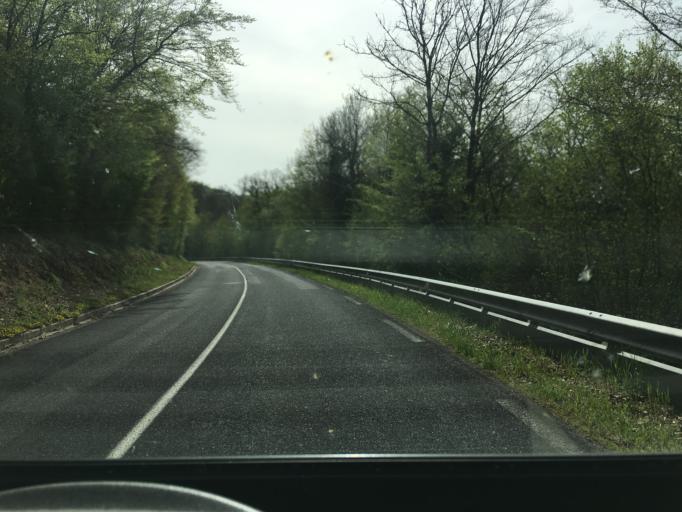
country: FR
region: Lorraine
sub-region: Departement de Meurthe-et-Moselle
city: Velaine-en-Haye
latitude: 48.6628
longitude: 6.0229
